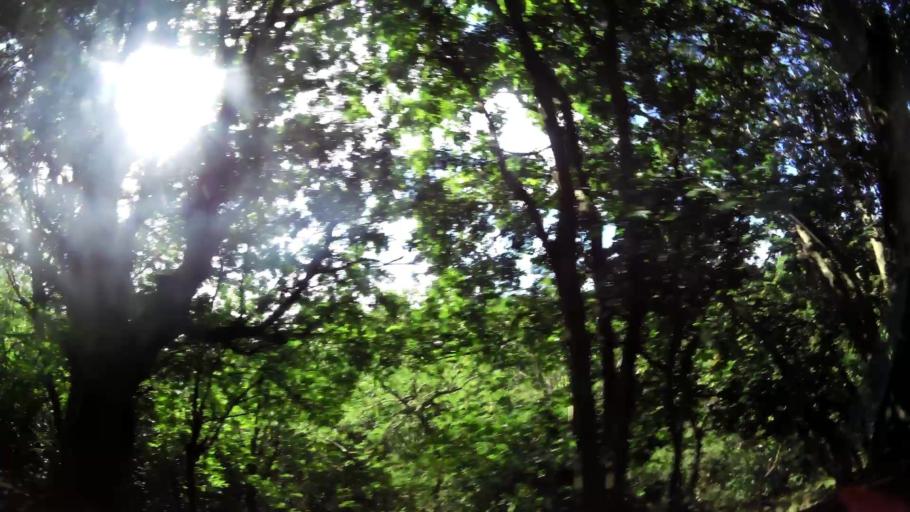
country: MS
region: Saint Peter
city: Saint Peters
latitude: 16.7472
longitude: -62.2192
